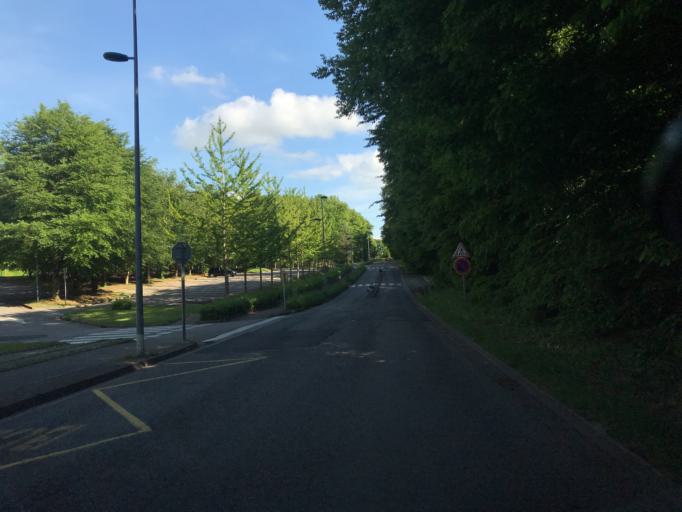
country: FR
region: Haute-Normandie
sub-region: Departement de l'Eure
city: Evreux
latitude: 49.0089
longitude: 1.1388
